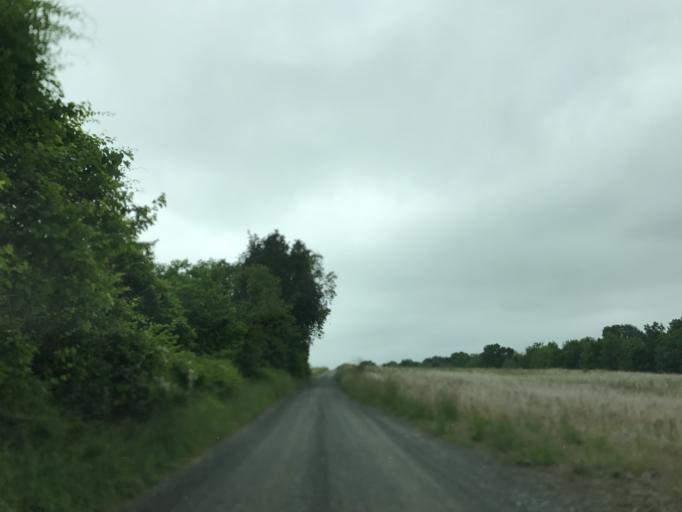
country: US
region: Maryland
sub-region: Harford County
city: Jarrettsville
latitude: 39.6795
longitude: -76.4598
